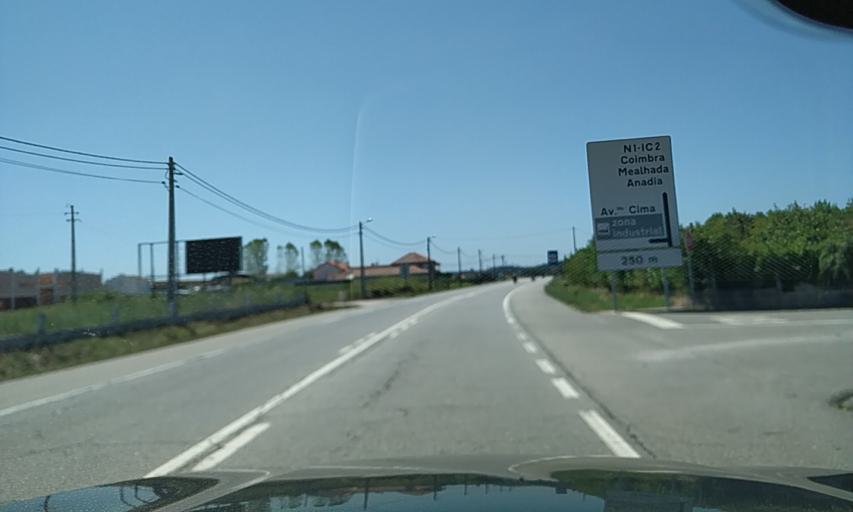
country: PT
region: Aveiro
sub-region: Anadia
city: Sangalhos
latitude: 40.4872
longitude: -8.4471
